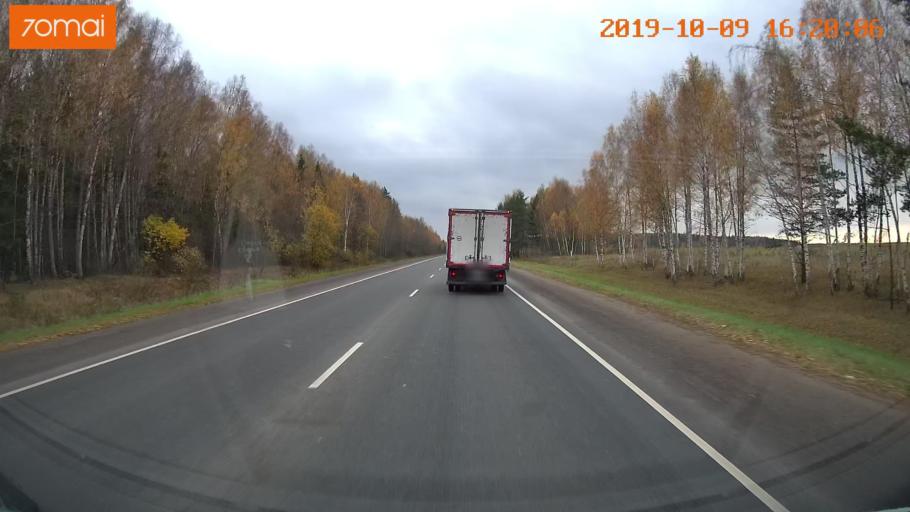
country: RU
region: Kostroma
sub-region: Kostromskoy Rayon
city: Kostroma
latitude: 57.7108
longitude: 40.8930
